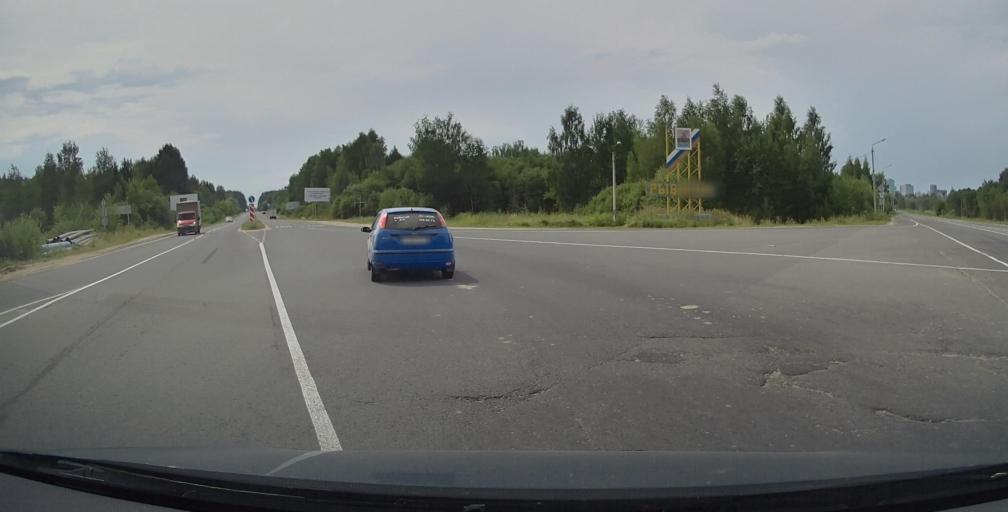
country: RU
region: Jaroslavl
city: Rybinsk
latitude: 58.0220
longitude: 38.9739
